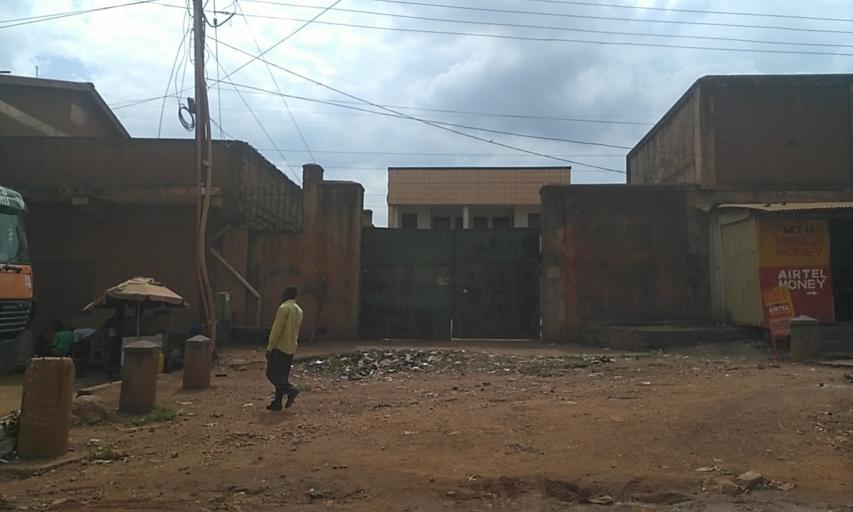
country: UG
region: Central Region
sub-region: Wakiso District
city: Kireka
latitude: 0.3370
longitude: 32.6196
